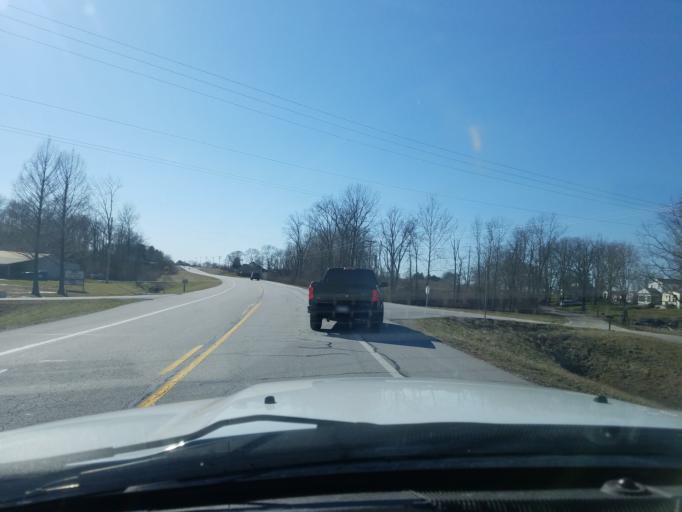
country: US
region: Indiana
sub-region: Johnson County
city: Franklin
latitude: 39.4951
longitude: -85.9645
